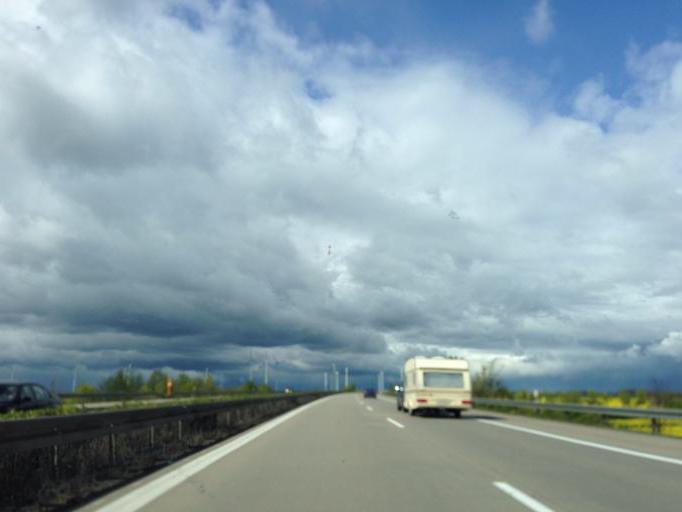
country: DE
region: Saxony-Anhalt
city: Nauendorf
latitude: 51.5951
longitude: 11.8727
